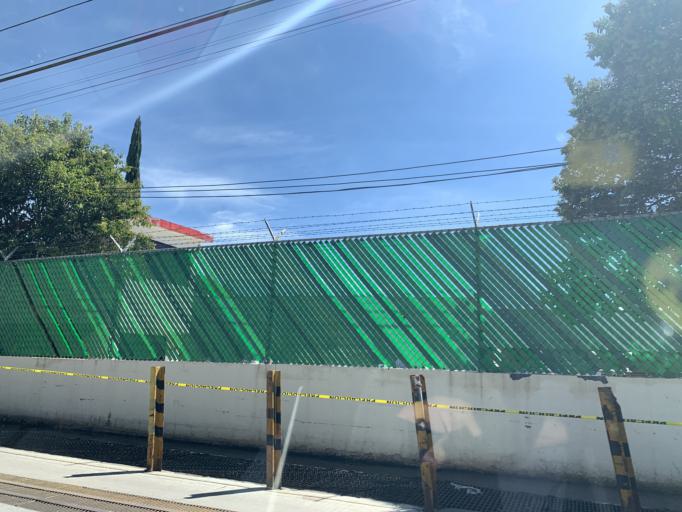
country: MX
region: Puebla
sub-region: Cuautlancingo
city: La Trinidad Chautenco
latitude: 19.0828
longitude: -98.2636
